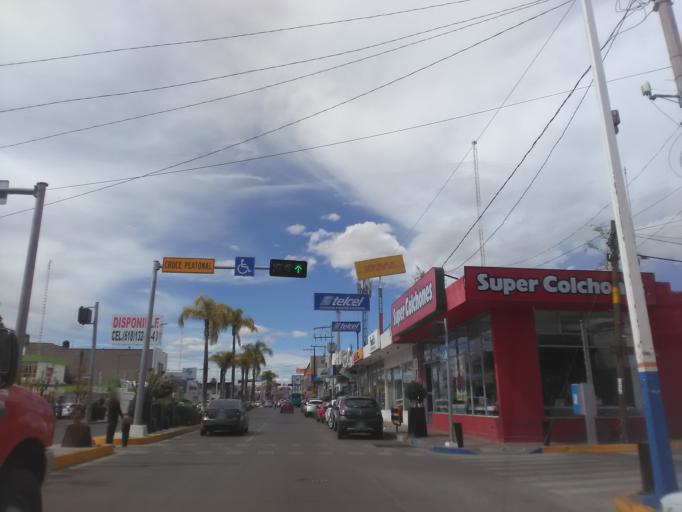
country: MX
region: Durango
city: Victoria de Durango
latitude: 24.0282
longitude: -104.6493
